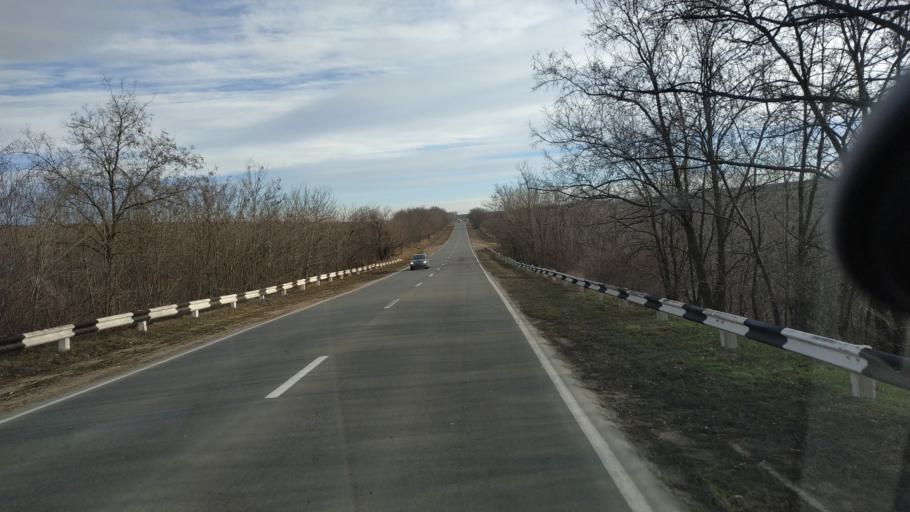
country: MD
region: Chisinau
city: Vadul lui Voda
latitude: 47.0813
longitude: 29.0349
